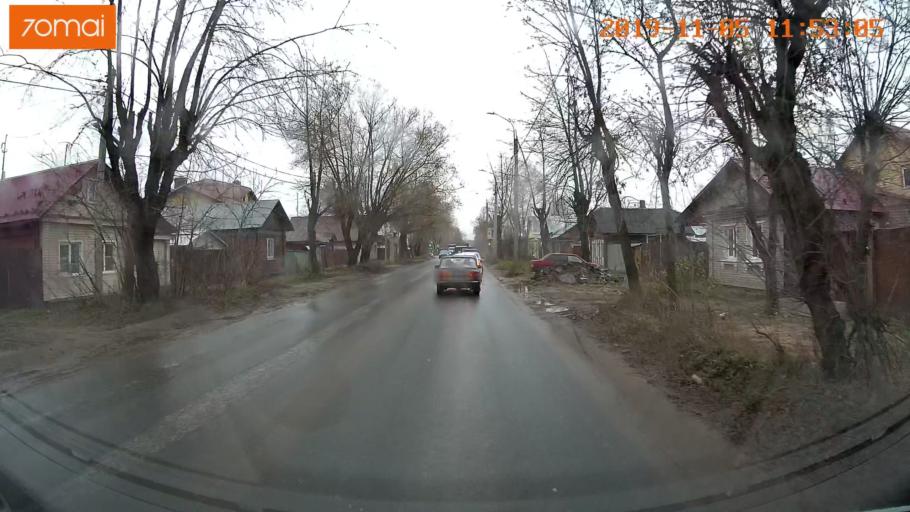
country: RU
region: Ivanovo
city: Bogorodskoye
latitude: 56.9963
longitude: 41.0302
